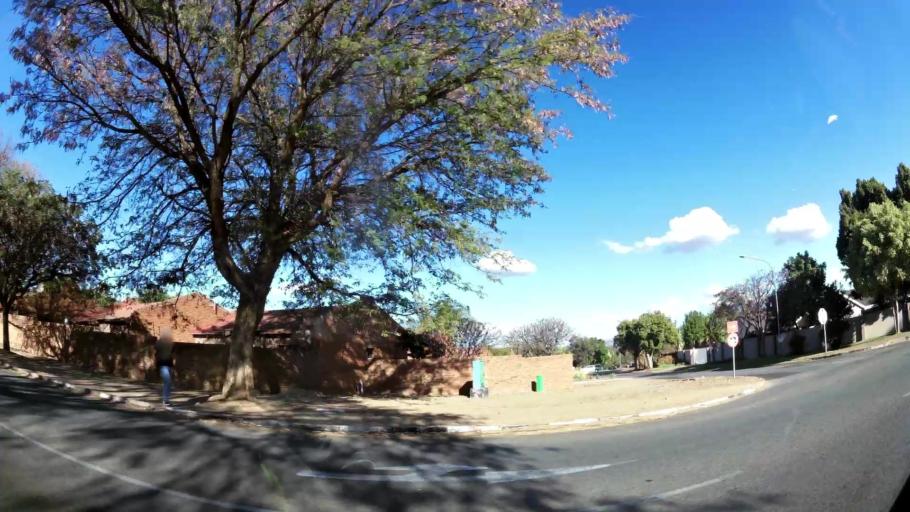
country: ZA
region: Limpopo
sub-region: Capricorn District Municipality
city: Polokwane
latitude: -23.9053
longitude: 29.4841
